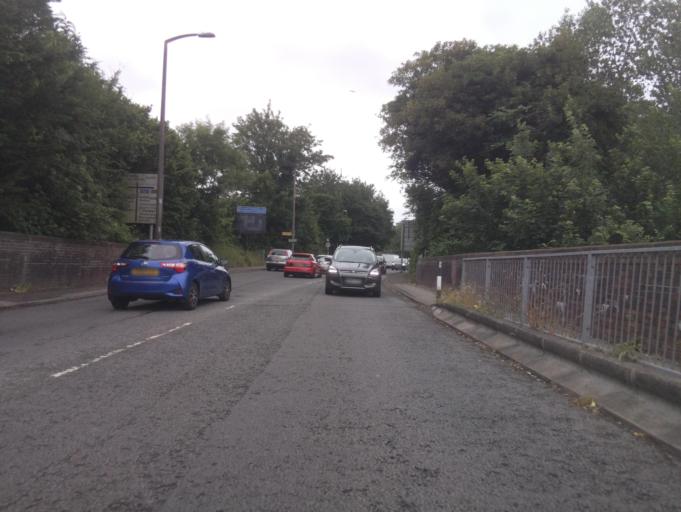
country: GB
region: Wales
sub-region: Vale of Glamorgan
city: Penarth
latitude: 51.4468
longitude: -3.1888
